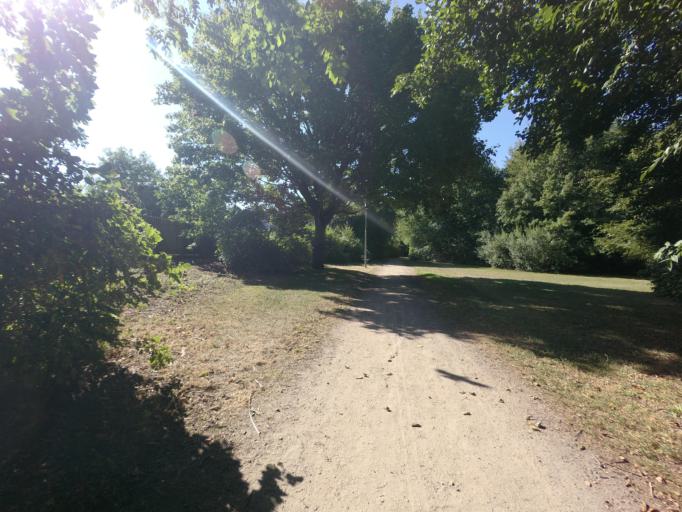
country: SE
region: Skane
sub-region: Trelleborgs Kommun
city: Skare
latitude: 55.4047
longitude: 13.0832
